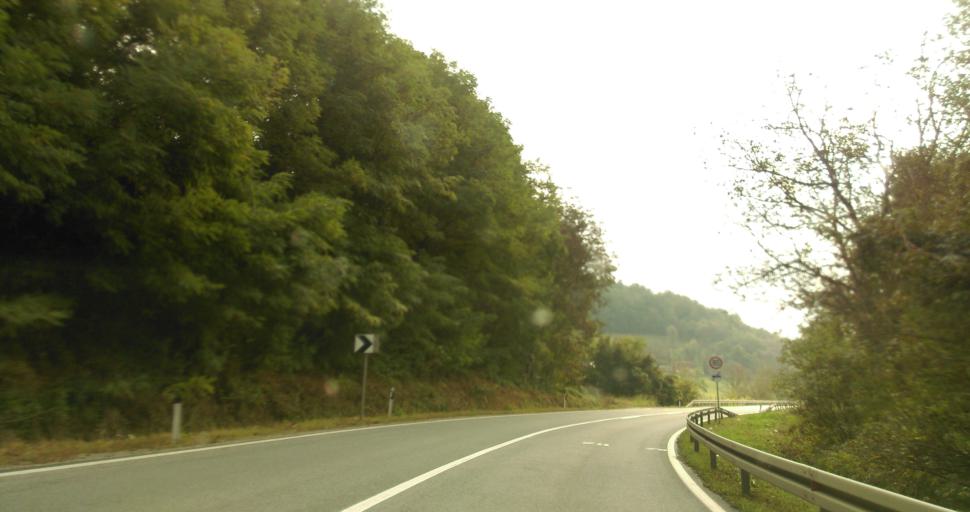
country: RS
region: Central Serbia
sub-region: Kolubarski Okrug
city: Ljig
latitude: 44.1970
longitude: 20.3025
